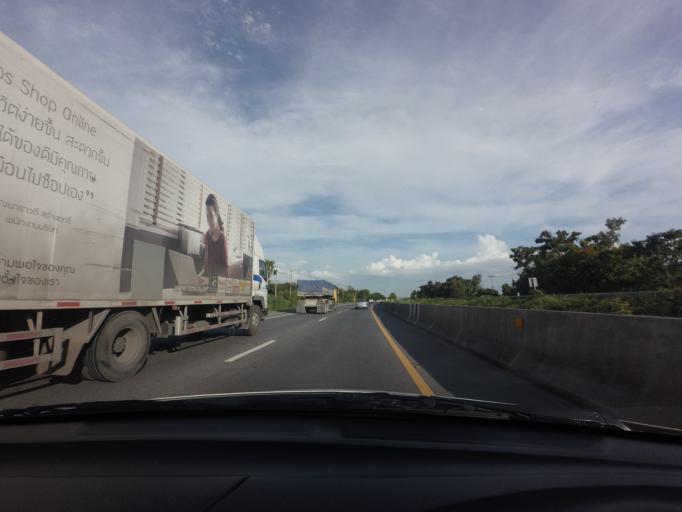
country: TH
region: Pathum Thani
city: Lat Lum Kaeo
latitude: 14.0007
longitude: 100.3736
